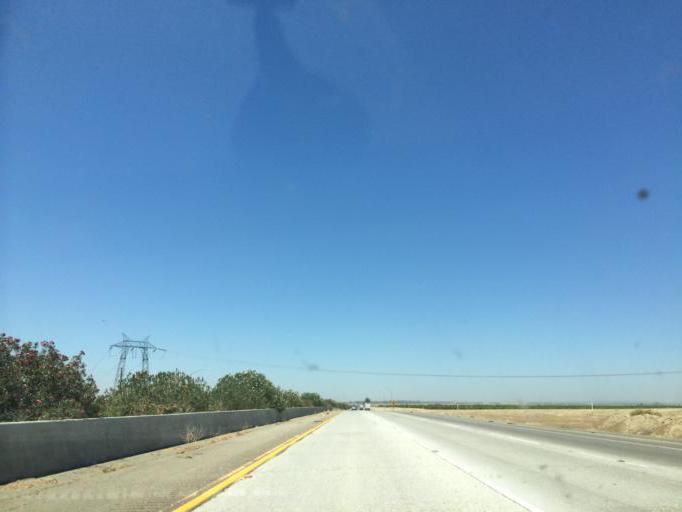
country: US
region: California
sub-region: Kern County
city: Weedpatch
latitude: 35.1228
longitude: -118.9884
